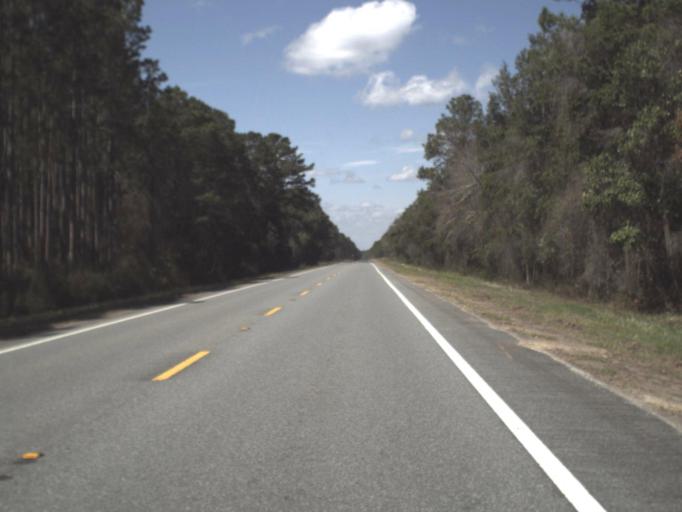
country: US
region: Florida
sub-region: Wakulla County
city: Crawfordville
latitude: 30.3115
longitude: -84.4361
